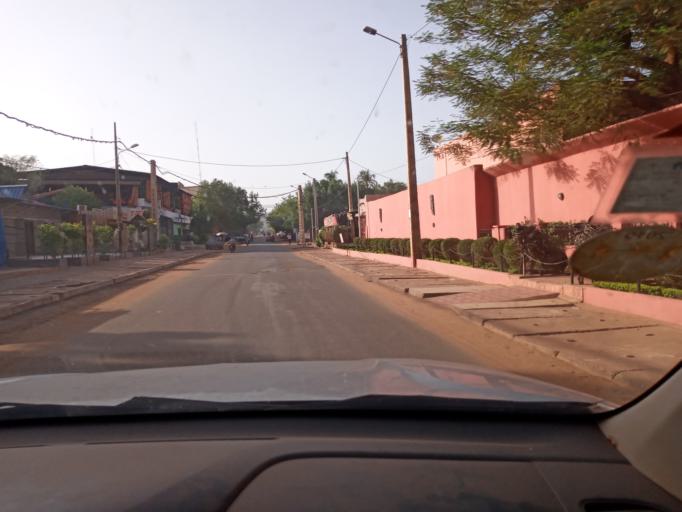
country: ML
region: Bamako
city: Bamako
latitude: 12.6593
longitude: -7.9718
